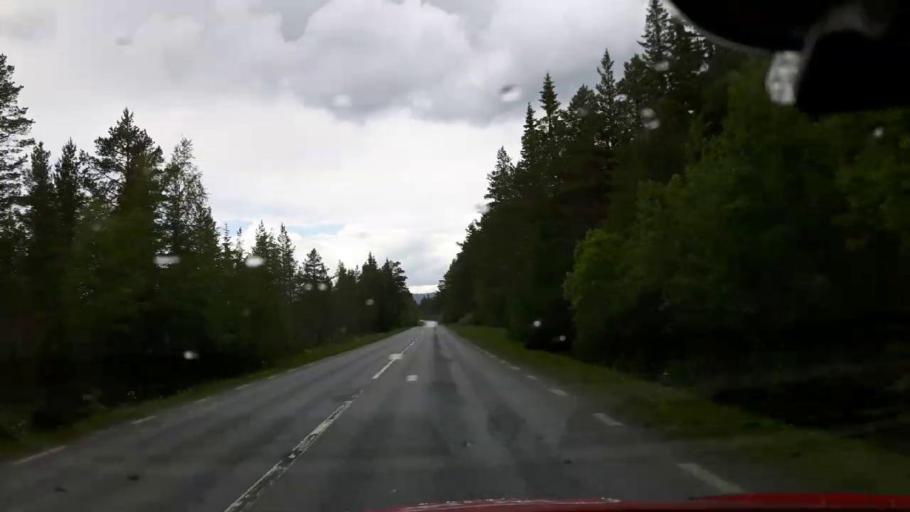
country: SE
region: Jaemtland
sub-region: Krokoms Kommun
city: Krokom
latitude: 63.4162
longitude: 14.2331
